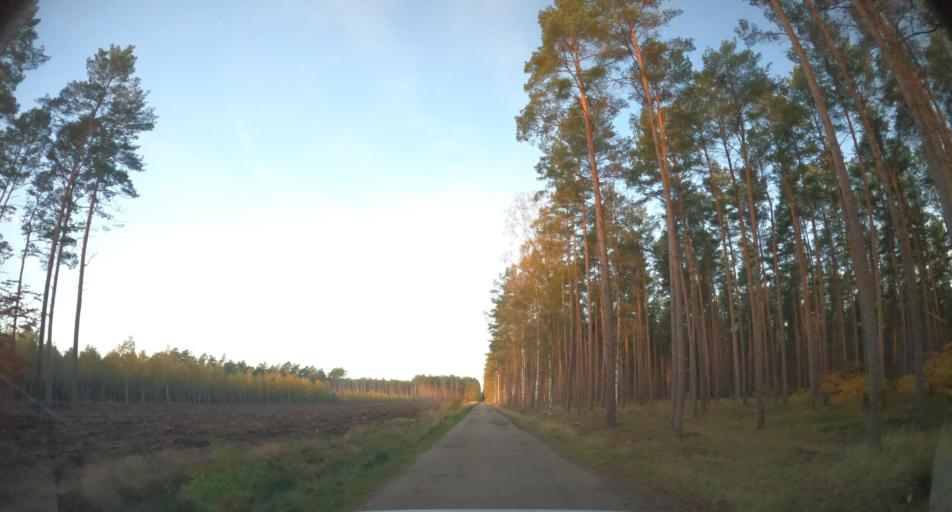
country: PL
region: West Pomeranian Voivodeship
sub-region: Powiat policki
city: Nowe Warpno
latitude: 53.6437
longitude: 14.3543
